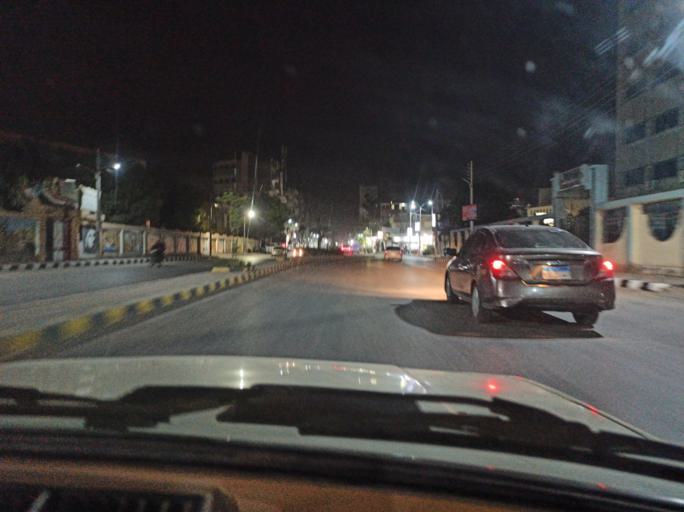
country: EG
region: Muhafazat Bani Suwayf
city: Bani Suwayf
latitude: 29.0821
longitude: 31.0989
